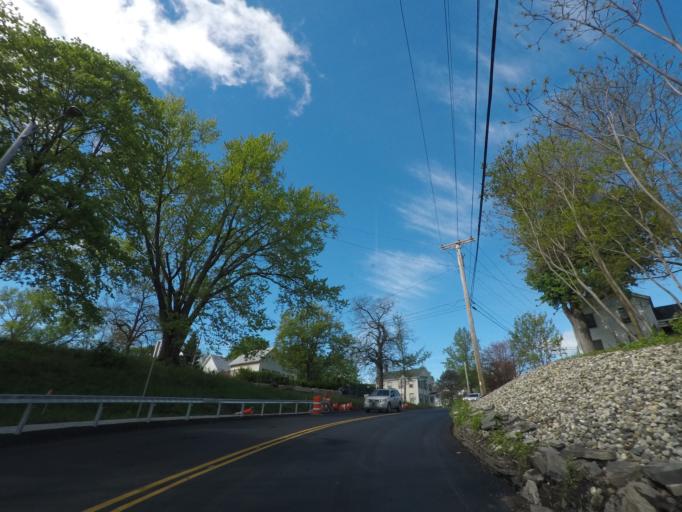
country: US
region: New York
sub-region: Albany County
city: Ravena
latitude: 42.4745
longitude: -73.7935
